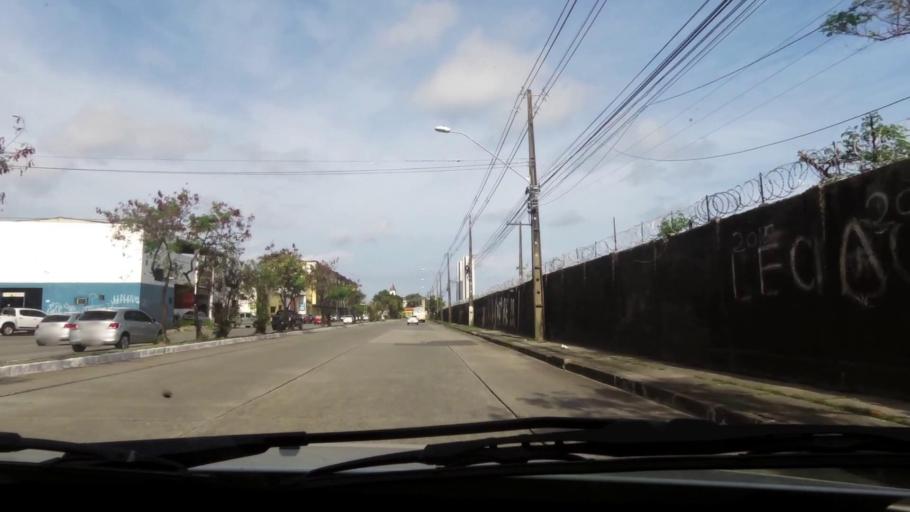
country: BR
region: Pernambuco
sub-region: Recife
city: Recife
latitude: -8.0732
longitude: -34.8841
